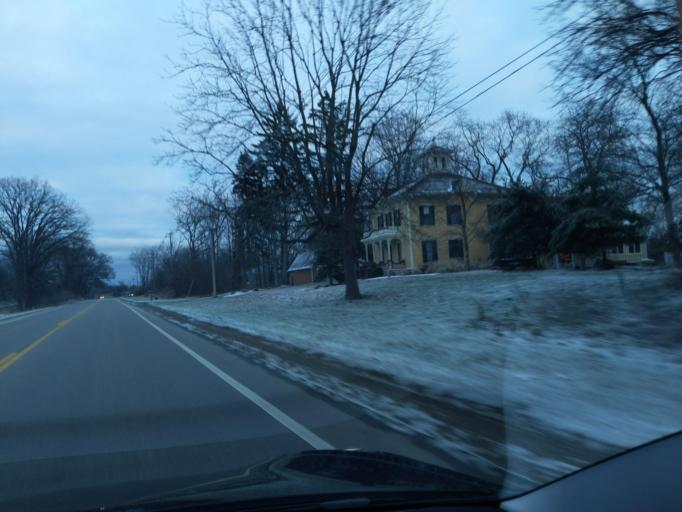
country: US
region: Michigan
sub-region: Jackson County
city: Spring Arbor
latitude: 42.2543
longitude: -84.4937
